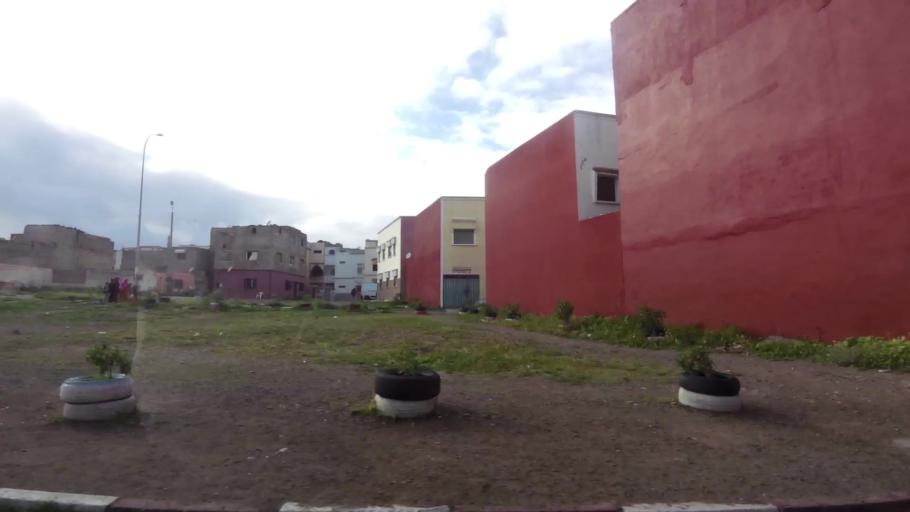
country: MA
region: Doukkala-Abda
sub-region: El-Jadida
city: El Jadida
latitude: 33.2433
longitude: -8.5283
